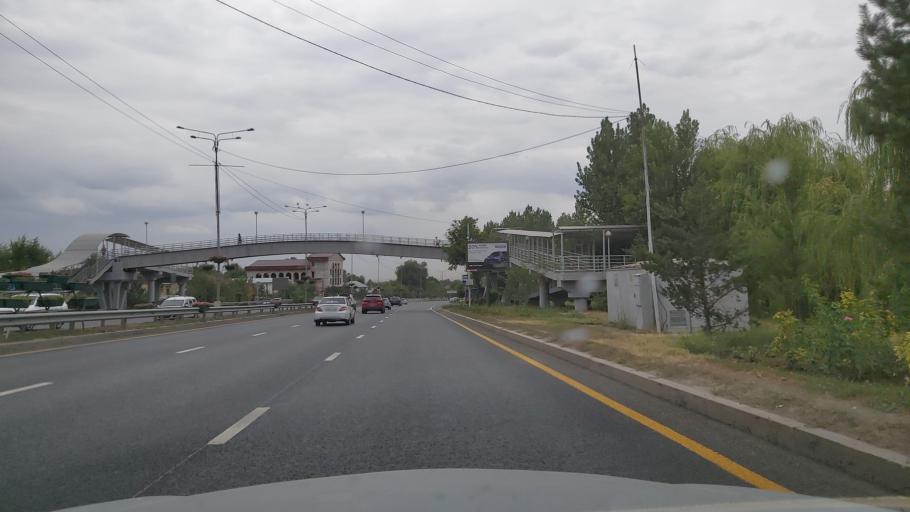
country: KZ
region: Almaty Qalasy
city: Almaty
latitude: 43.2718
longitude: 76.9856
